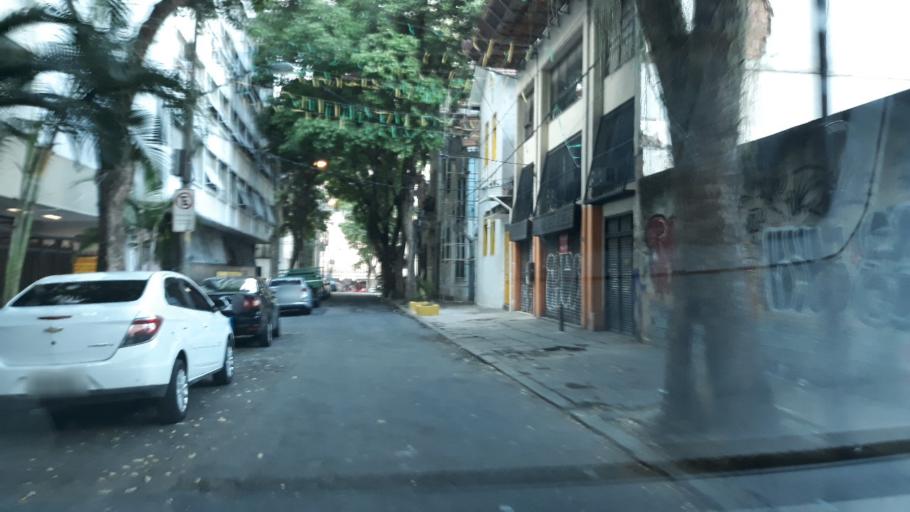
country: BR
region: Rio de Janeiro
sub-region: Rio De Janeiro
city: Rio de Janeiro
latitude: -22.9174
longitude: -43.1779
